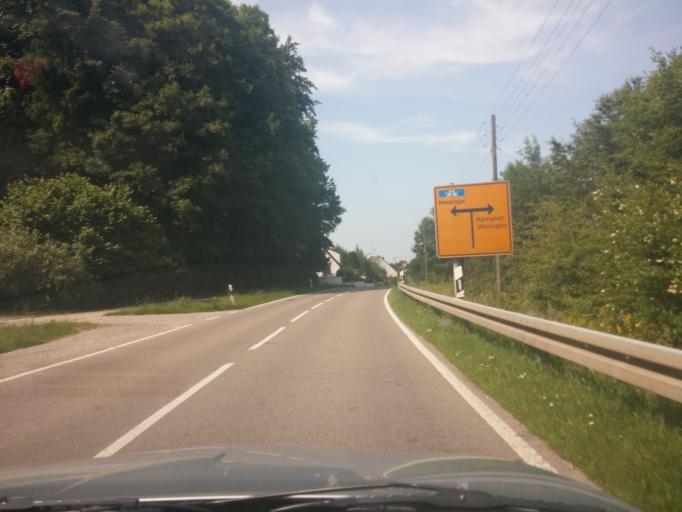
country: DE
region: Bavaria
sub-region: Swabia
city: Memmingen
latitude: 47.9570
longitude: 10.1827
